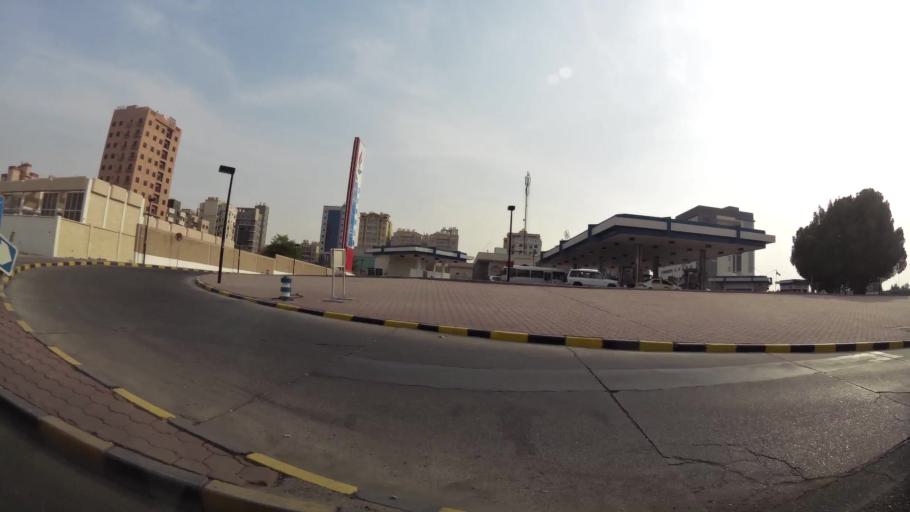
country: KW
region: Al Farwaniyah
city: Al Farwaniyah
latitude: 29.2970
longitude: 47.9672
